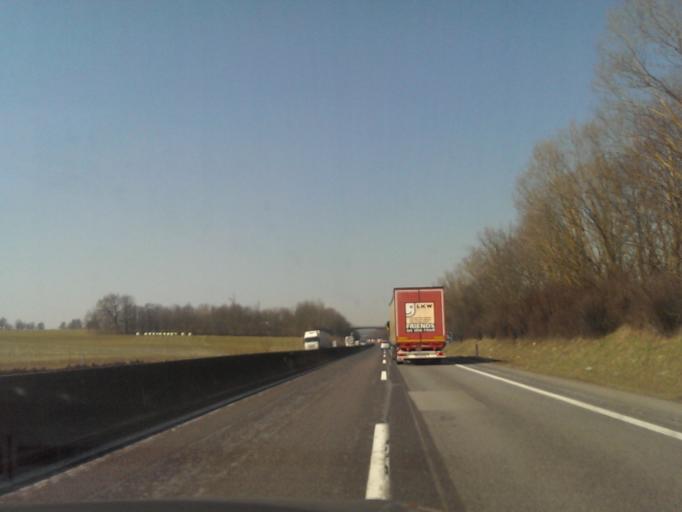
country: AT
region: Upper Austria
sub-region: Politischer Bezirk Vocklabruck
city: Wolfsegg am Hausruck
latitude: 48.2153
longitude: 13.6244
